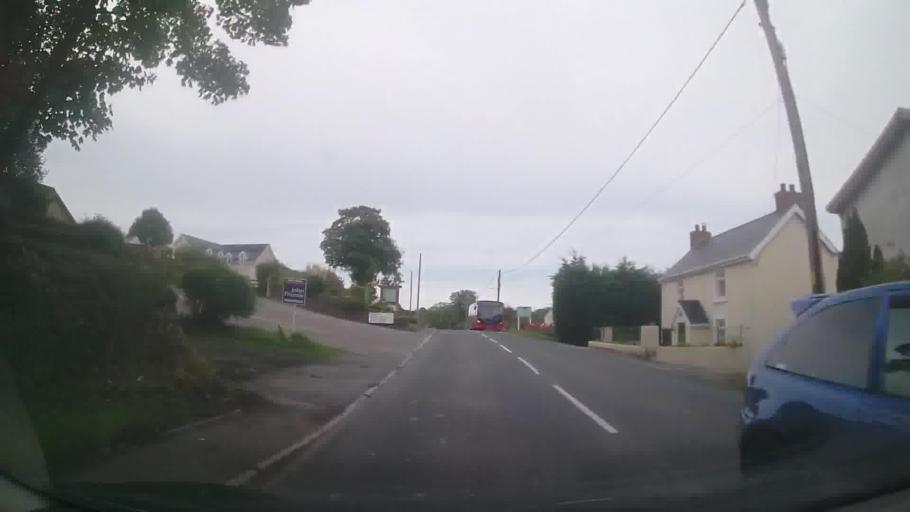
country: GB
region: Wales
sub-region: Pembrokeshire
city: Kilgetty
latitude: 51.7358
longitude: -4.7272
